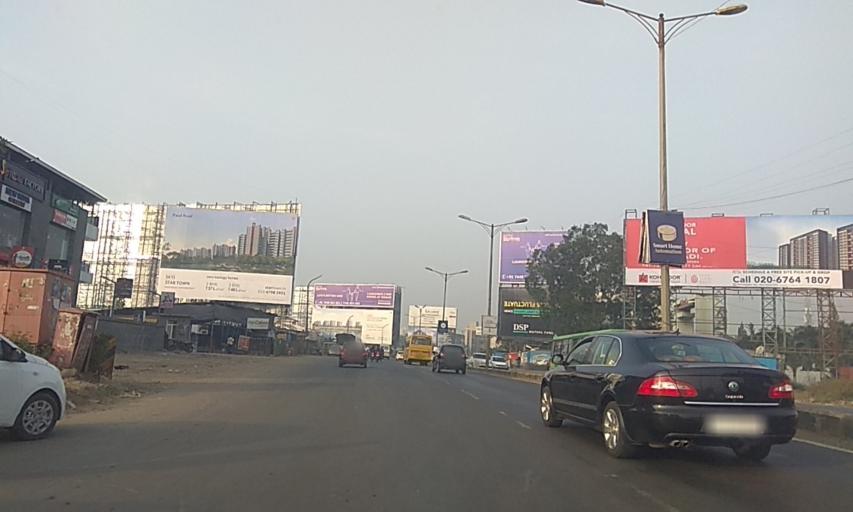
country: IN
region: Maharashtra
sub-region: Pune Division
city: Pimpri
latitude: 18.5913
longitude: 73.7531
